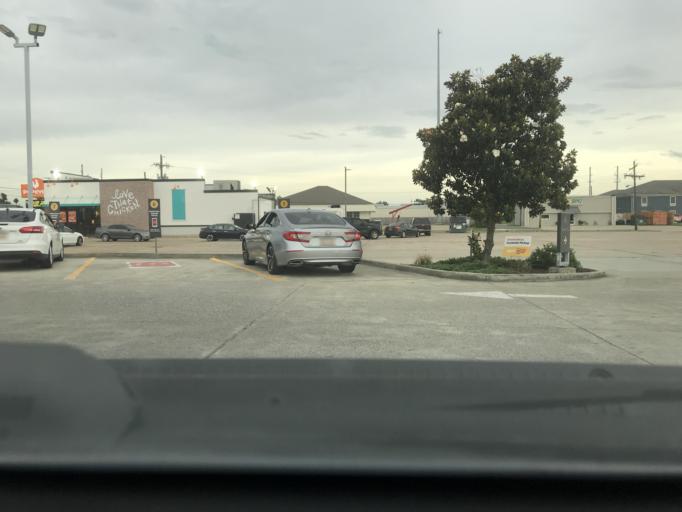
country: US
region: Louisiana
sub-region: Calcasieu Parish
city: Westlake
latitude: 30.2541
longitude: -93.2586
